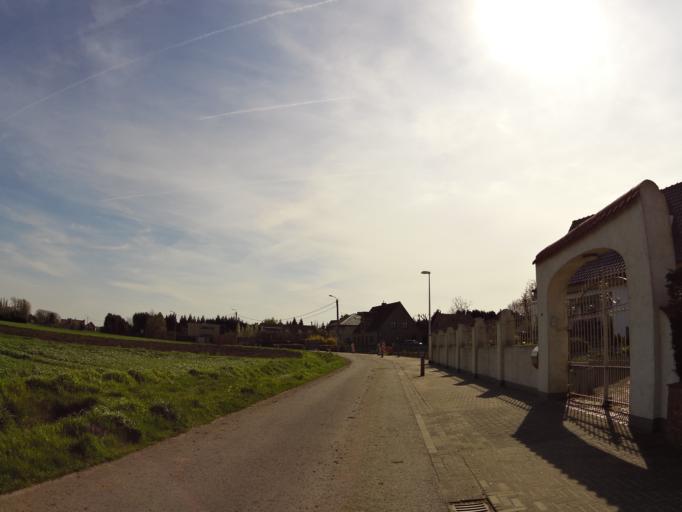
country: BE
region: Flanders
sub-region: Provincie West-Vlaanderen
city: Oudenburg
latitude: 51.1689
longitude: 3.0359
